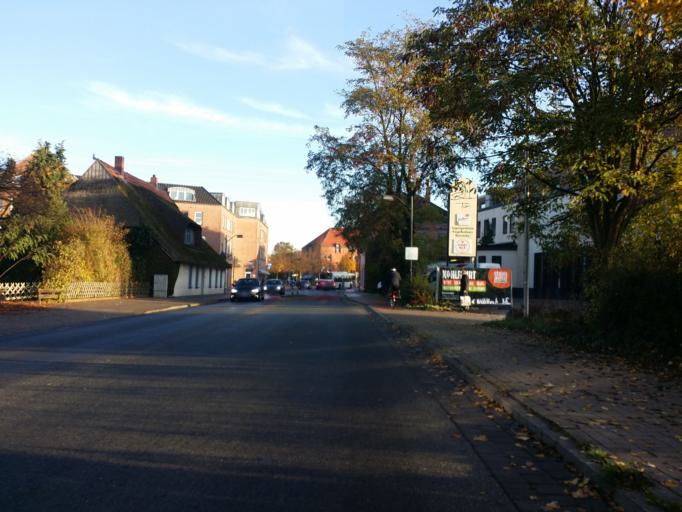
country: DE
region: Lower Saxony
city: Stuhr
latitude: 53.0108
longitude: 8.7883
